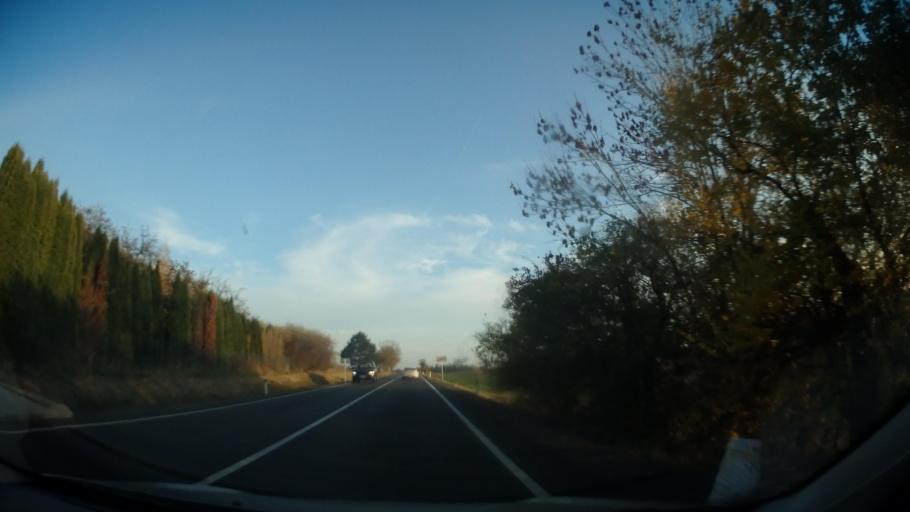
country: CZ
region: Central Bohemia
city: Postupice
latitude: 49.7449
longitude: 14.7971
